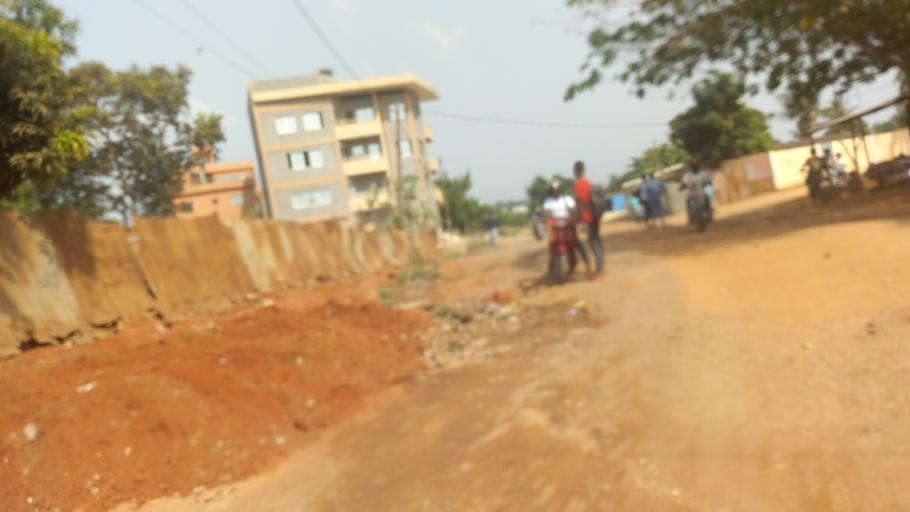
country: TG
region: Maritime
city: Lome
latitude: 6.1680
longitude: 1.2055
